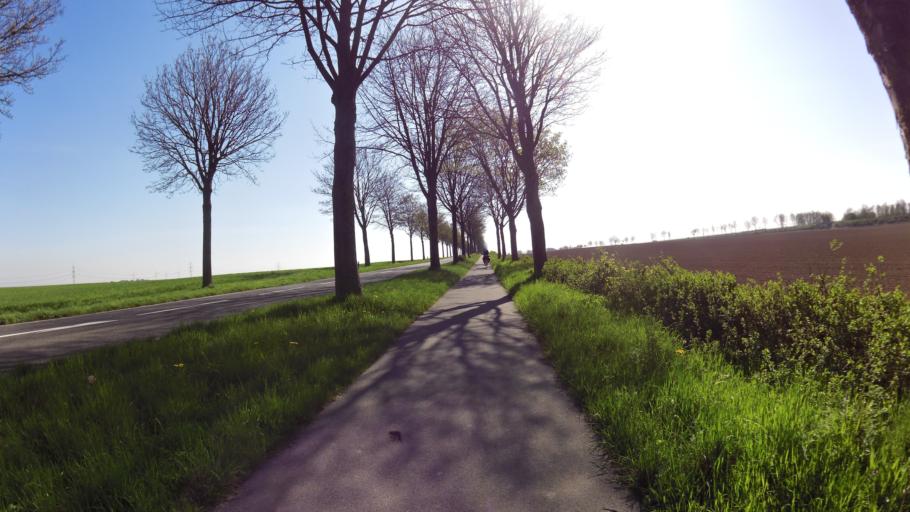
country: DE
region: North Rhine-Westphalia
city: Geilenkirchen
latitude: 50.9576
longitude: 6.1453
